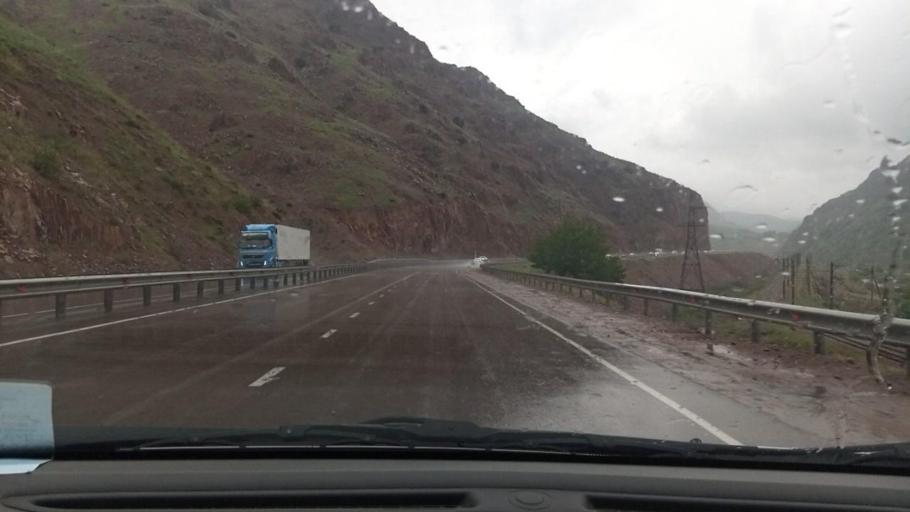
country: UZ
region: Toshkent
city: Angren
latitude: 41.1142
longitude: 70.3399
